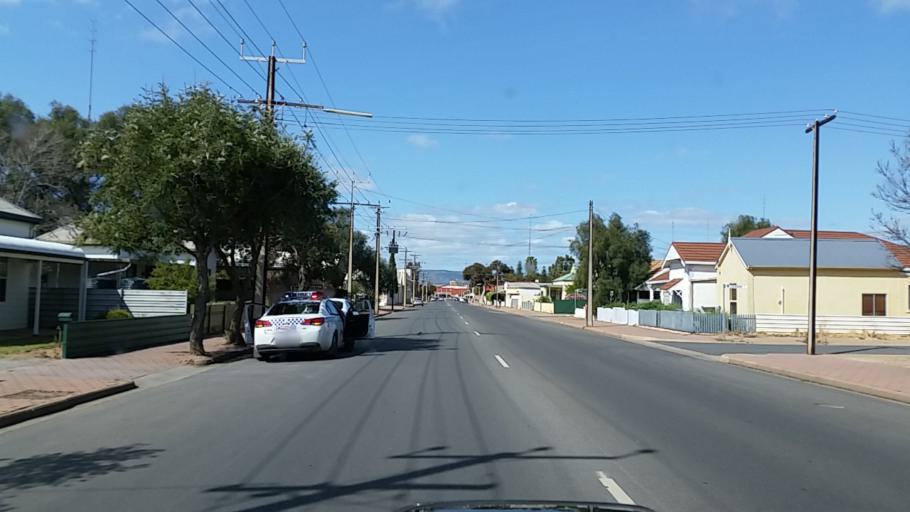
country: AU
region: South Australia
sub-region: Port Pirie City and Dists
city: Port Pirie
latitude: -33.1772
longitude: 137.9993
